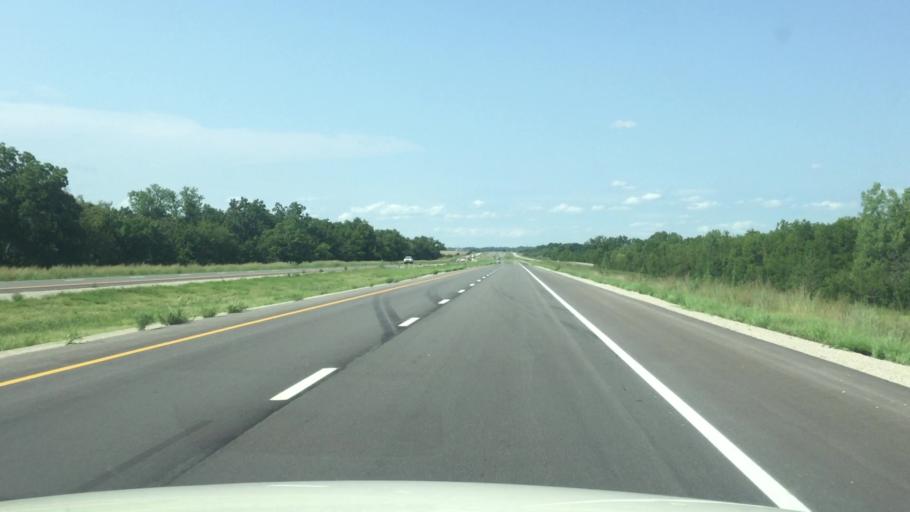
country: US
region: Kansas
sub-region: Linn County
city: La Cygne
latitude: 38.3013
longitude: -94.6773
